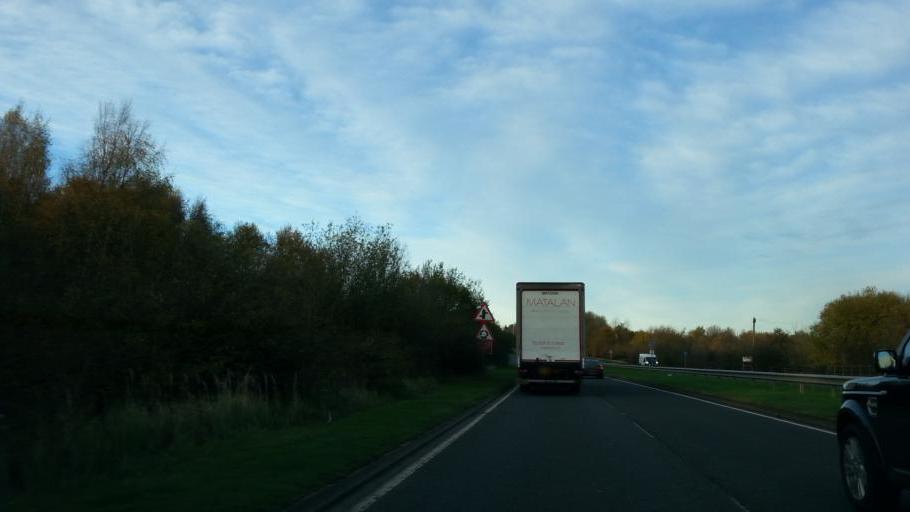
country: GB
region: England
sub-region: Northamptonshire
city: Corby
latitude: 52.4912
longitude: -0.6534
